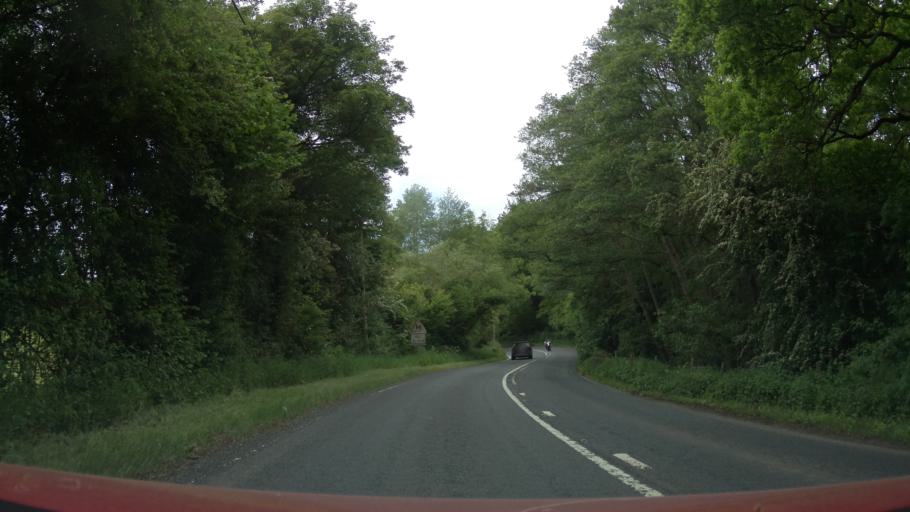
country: GB
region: England
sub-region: Herefordshire
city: Yatton
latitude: 51.9784
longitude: -2.5136
